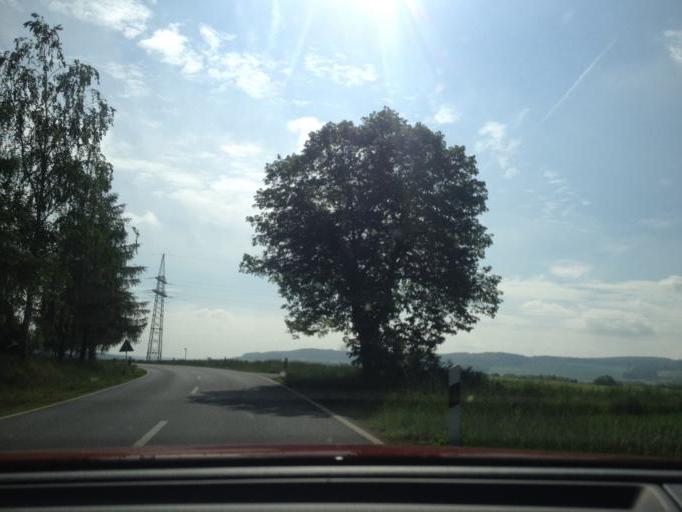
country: DE
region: Bavaria
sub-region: Upper Franconia
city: Thiersheim
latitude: 50.0331
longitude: 12.1418
